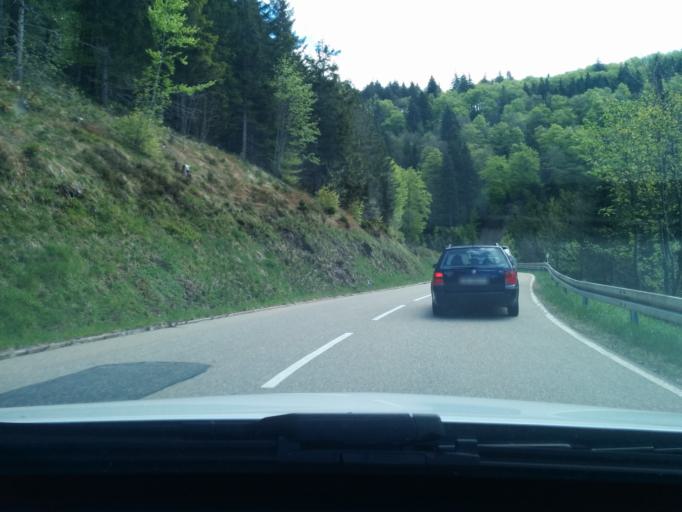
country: DE
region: Baden-Wuerttemberg
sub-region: Freiburg Region
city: Horben
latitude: 47.9136
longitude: 7.8941
